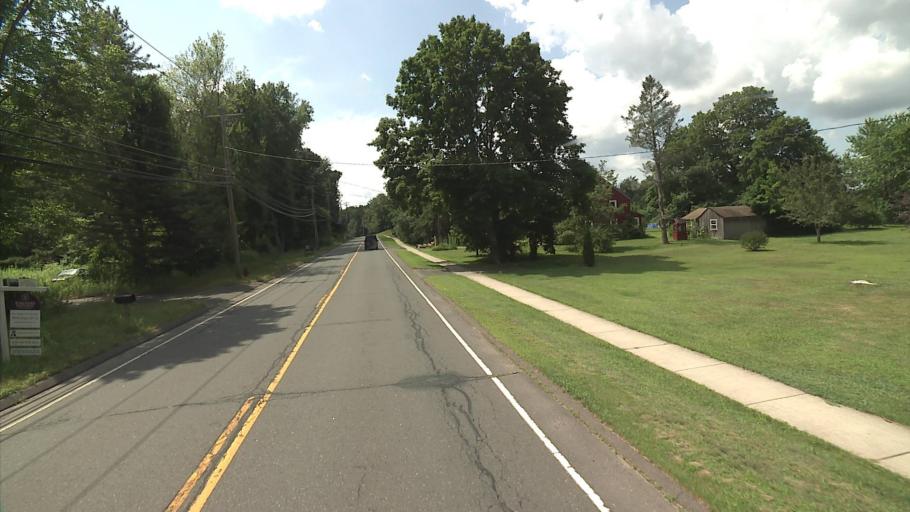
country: US
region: Connecticut
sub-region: Hartford County
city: Glastonbury Center
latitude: 41.6422
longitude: -72.6058
